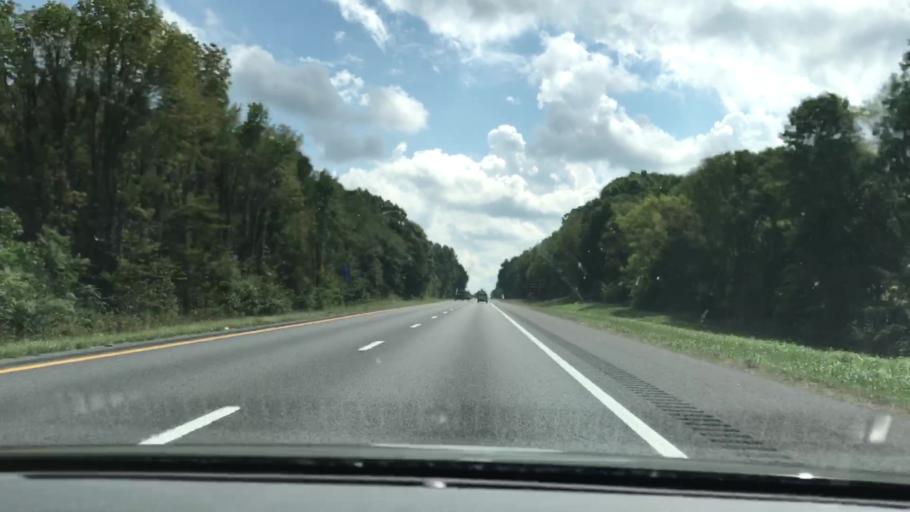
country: US
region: Tennessee
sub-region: Montgomery County
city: Clarksville
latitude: 36.5661
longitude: -87.2553
